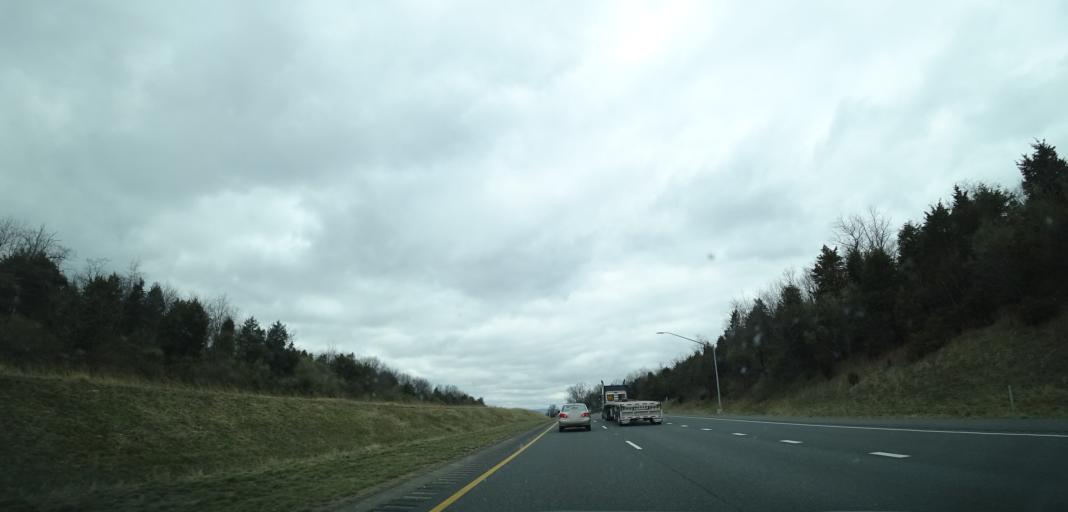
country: US
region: Maryland
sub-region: Washington County
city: Wilson-Conococheague
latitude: 39.6334
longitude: -77.8143
